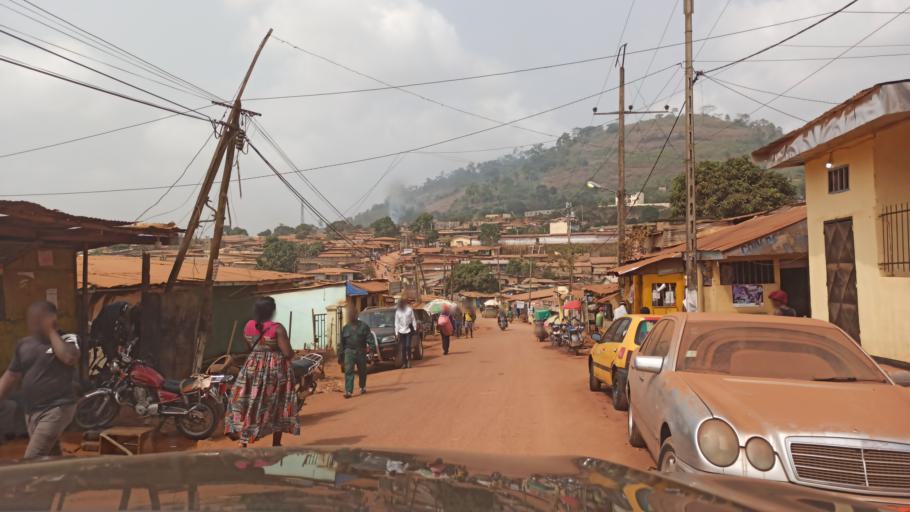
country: CM
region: Centre
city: Yaounde
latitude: 3.8853
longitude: 11.4912
